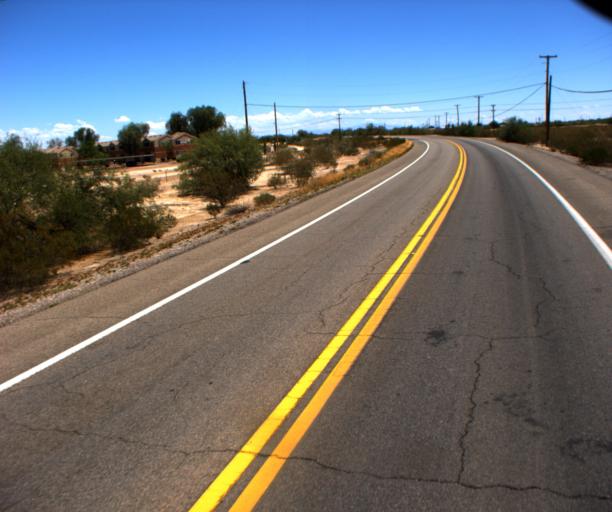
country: US
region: Arizona
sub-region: Pinal County
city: Florence
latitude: 33.0184
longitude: -111.3868
